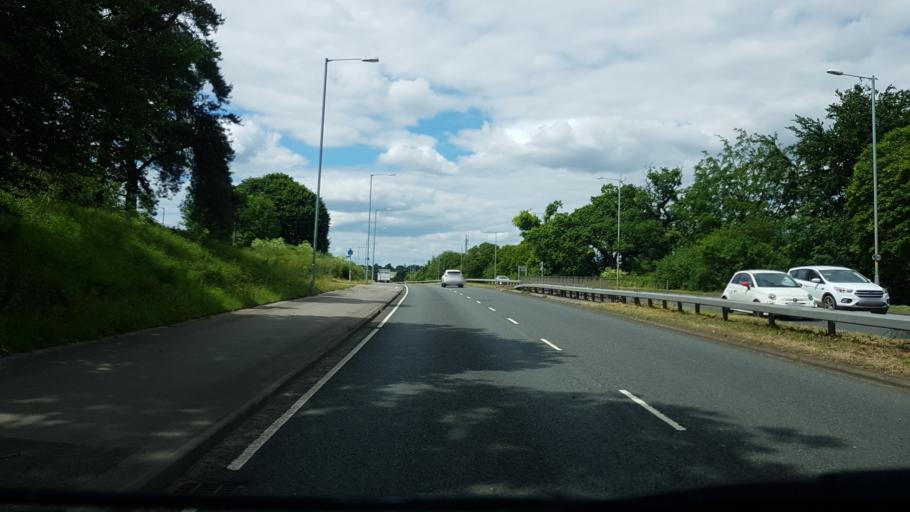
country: GB
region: England
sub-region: Worcestershire
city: Droitwich
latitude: 52.2777
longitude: -2.1614
